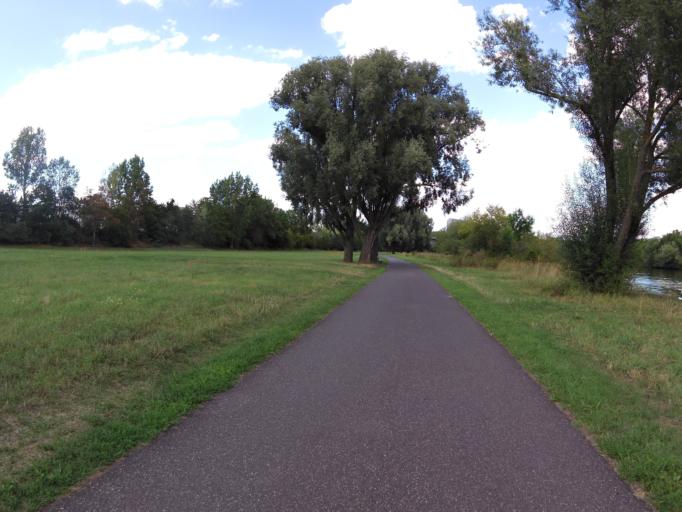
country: DE
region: Bavaria
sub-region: Regierungsbezirk Unterfranken
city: Schweinfurt
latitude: 50.0315
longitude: 10.2197
